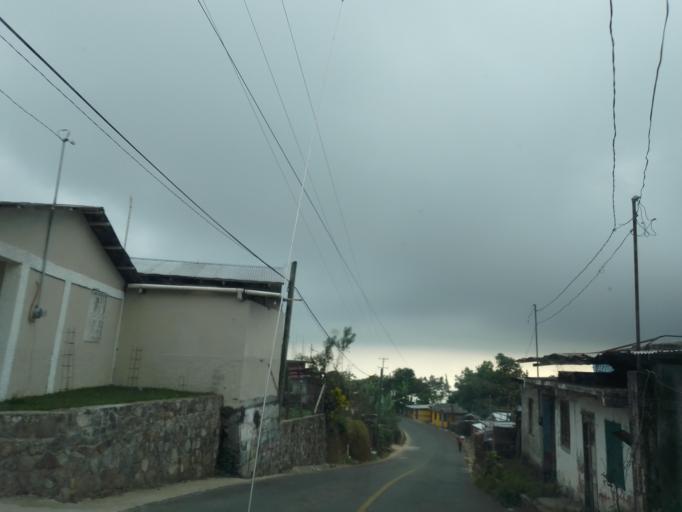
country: MX
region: Chiapas
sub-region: Union Juarez
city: Santo Domingo
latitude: 15.0745
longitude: -92.0805
